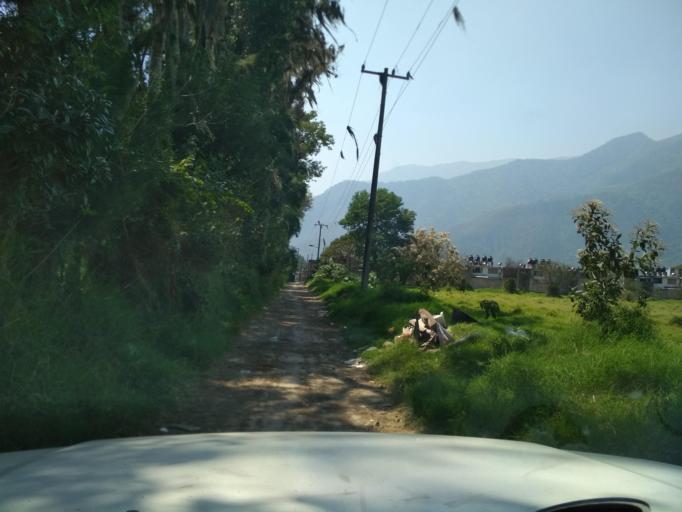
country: MX
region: Veracruz
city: Rio Blanco
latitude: 18.8452
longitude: -97.1235
